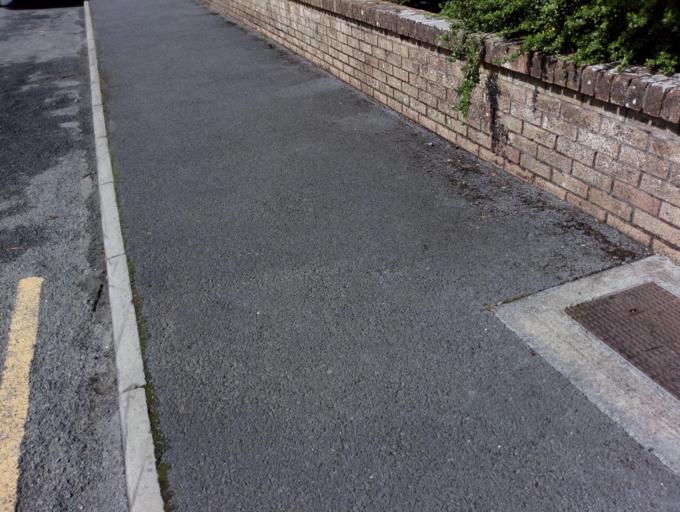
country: IE
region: Connaught
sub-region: County Galway
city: Gaillimh
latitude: 53.2620
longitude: -9.0764
